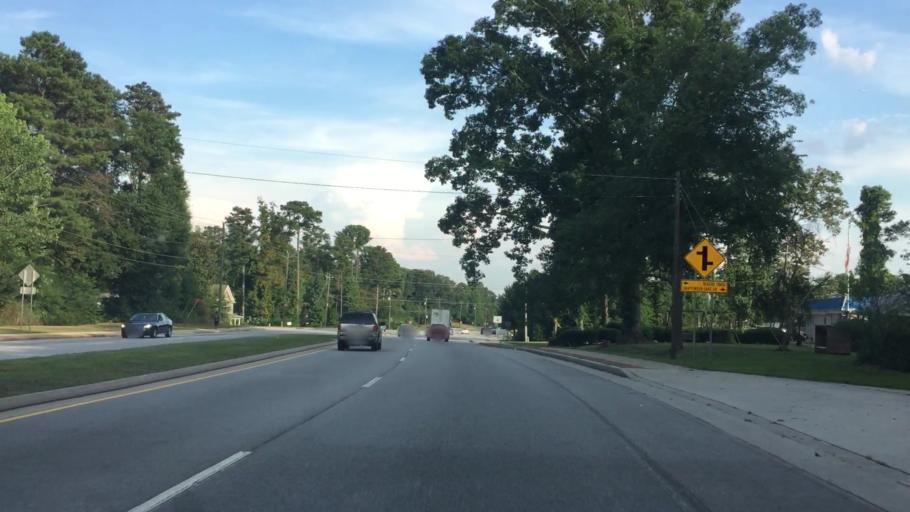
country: US
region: Georgia
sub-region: DeKalb County
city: Panthersville
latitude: 33.6967
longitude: -84.2062
